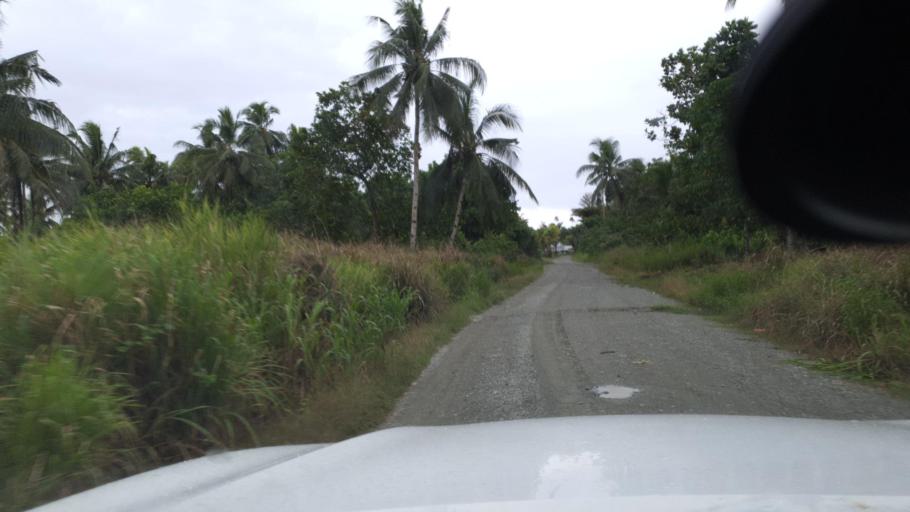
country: SB
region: Central Province
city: Tulaghi
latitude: -9.4511
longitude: 160.3919
